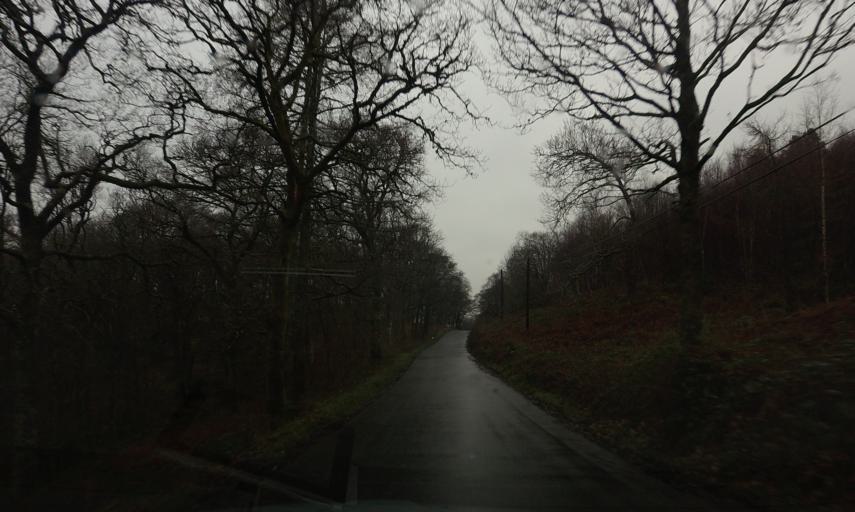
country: GB
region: Scotland
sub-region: West Dunbartonshire
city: Balloch
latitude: 56.1217
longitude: -4.5944
